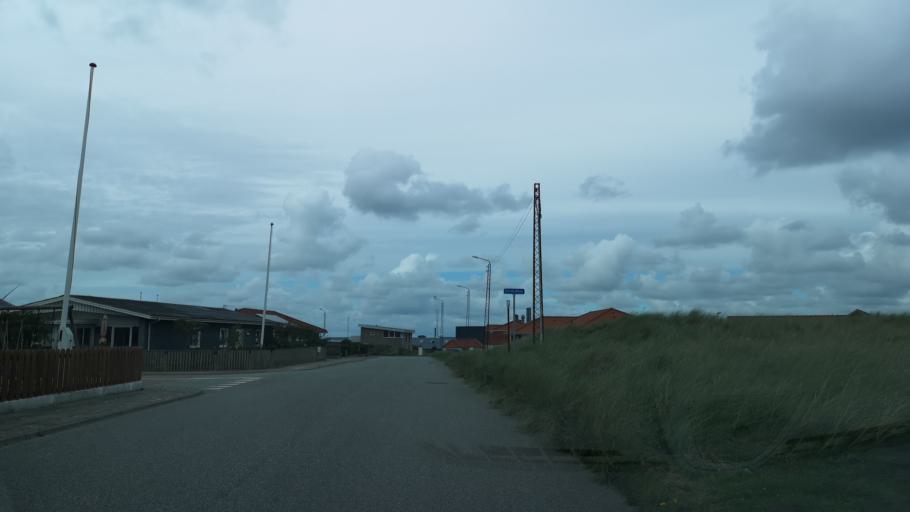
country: DK
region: Central Jutland
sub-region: Ringkobing-Skjern Kommune
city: Hvide Sande
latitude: 55.9965
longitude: 8.1310
